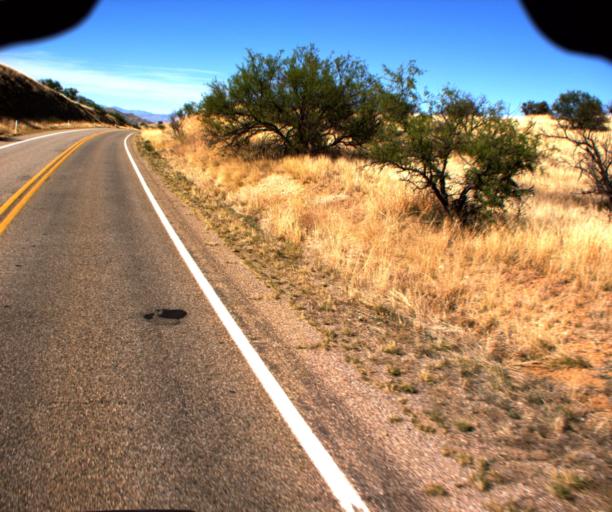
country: US
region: Arizona
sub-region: Pima County
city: Corona de Tucson
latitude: 31.8145
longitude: -110.7121
